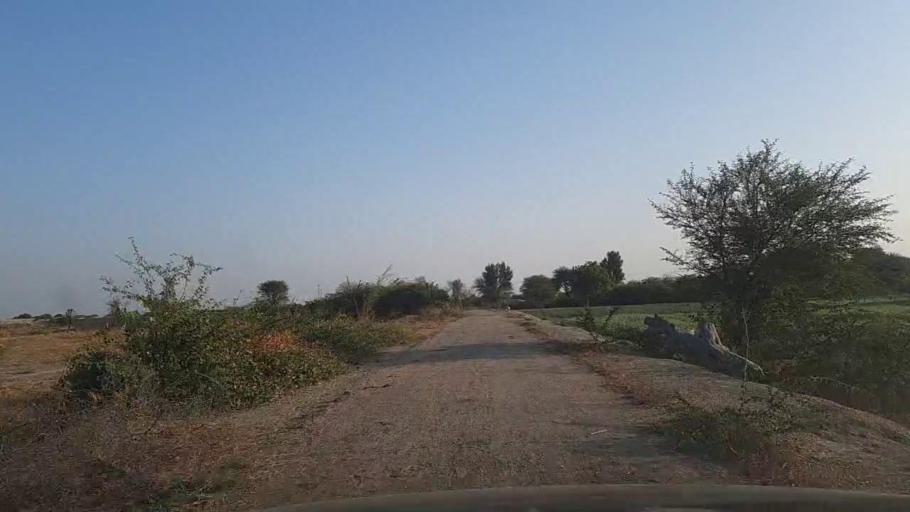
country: PK
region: Sindh
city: Naukot
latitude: 24.8929
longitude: 69.3455
